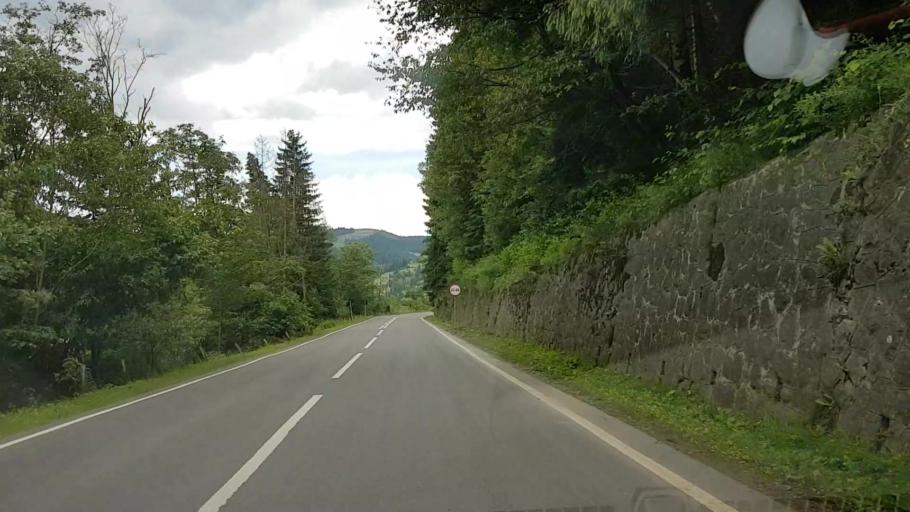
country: RO
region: Neamt
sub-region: Comuna Poiana Teiului
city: Poiana Teiului
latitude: 47.0927
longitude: 25.9519
